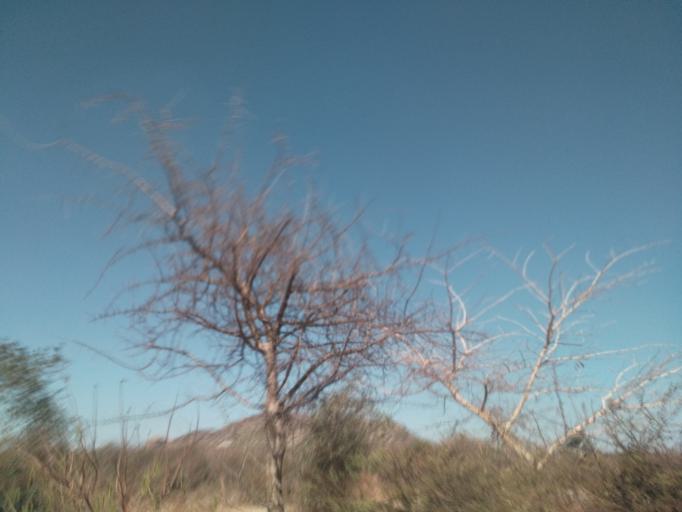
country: TZ
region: Dodoma
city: Dodoma
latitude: -6.1836
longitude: 35.7012
